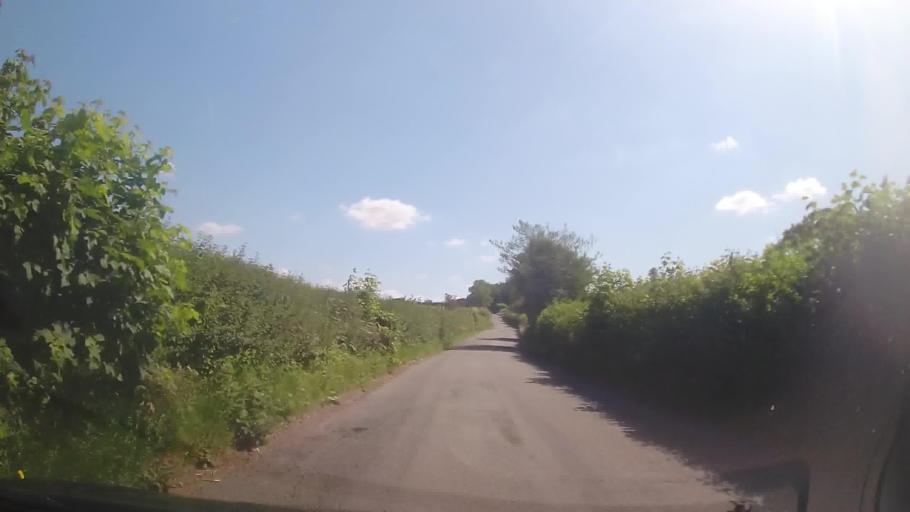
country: GB
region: England
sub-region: Herefordshire
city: Withington
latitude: 52.0742
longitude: -2.6358
